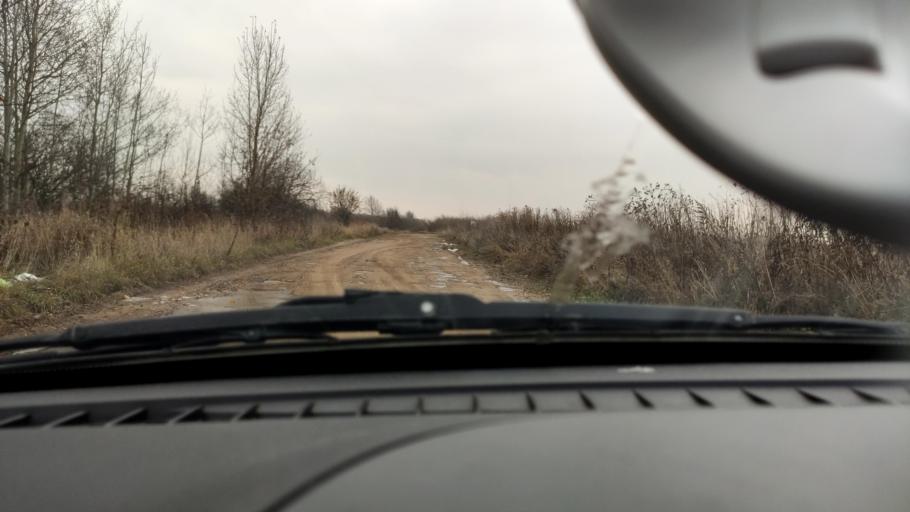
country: RU
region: Perm
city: Kondratovo
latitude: 57.9877
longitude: 56.0793
